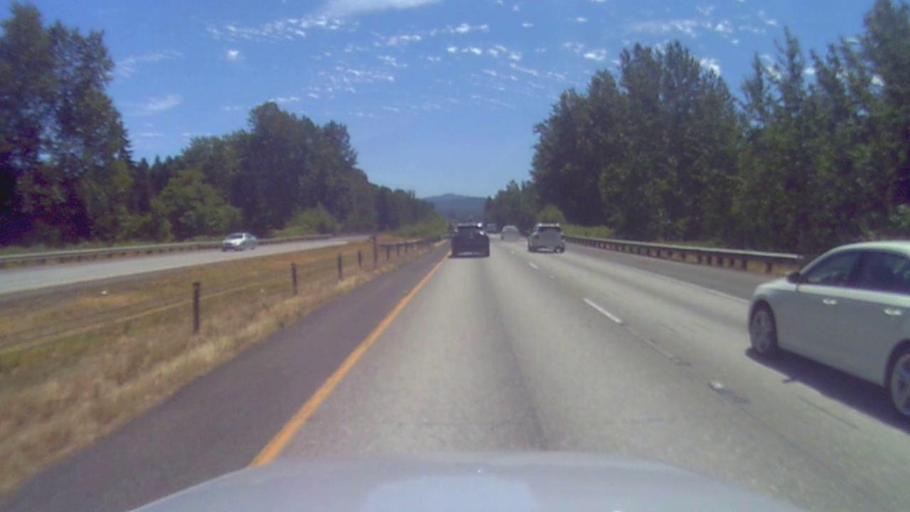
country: US
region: Washington
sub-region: Whatcom County
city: Bellingham
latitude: 48.7783
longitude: -122.4711
